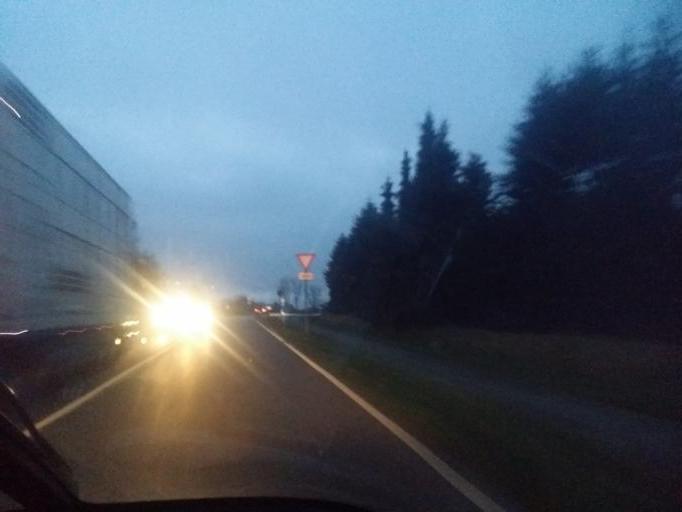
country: DE
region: Schleswig-Holstein
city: Poschendorf
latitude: 54.0336
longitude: 9.4785
